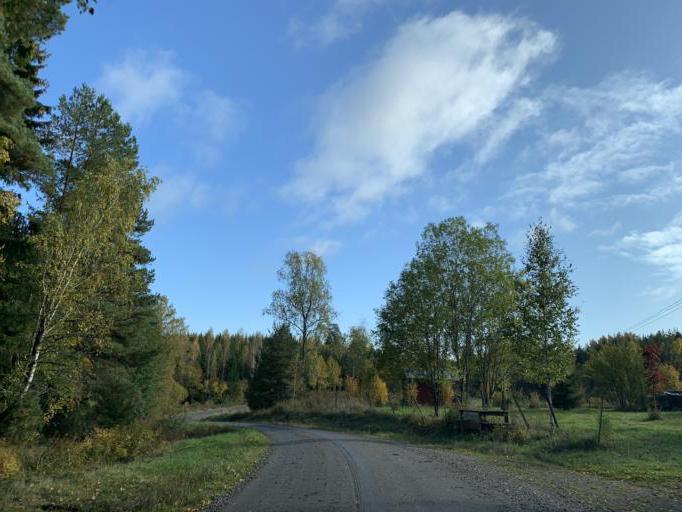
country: SE
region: Soedermanland
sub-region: Eskilstuna Kommun
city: Kvicksund
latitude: 59.3921
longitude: 16.2281
